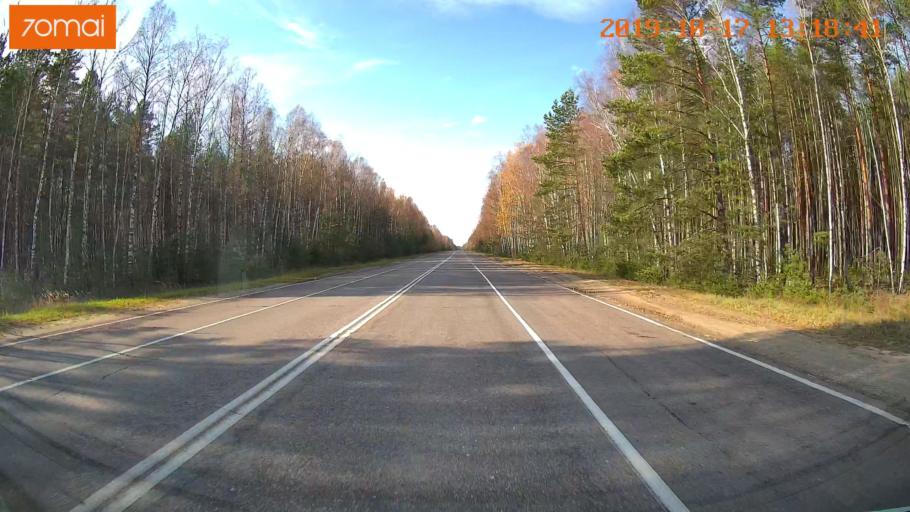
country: RU
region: Rjazan
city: Gus'-Zheleznyy
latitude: 55.0645
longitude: 41.0921
